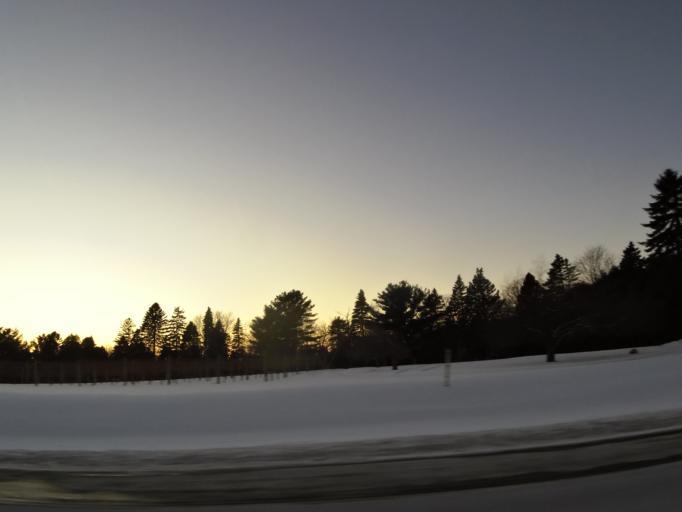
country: US
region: Minnesota
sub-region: Washington County
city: Lake Elmo
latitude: 45.0430
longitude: -92.8631
